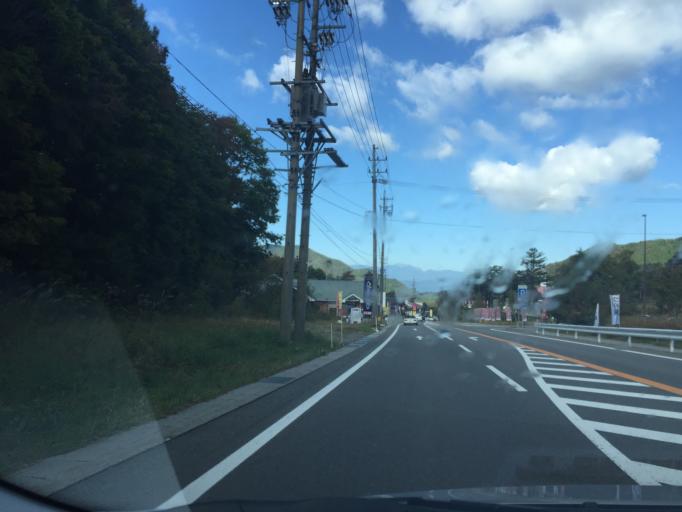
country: JP
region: Gifu
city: Nakatsugawa
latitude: 35.3518
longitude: 137.6681
